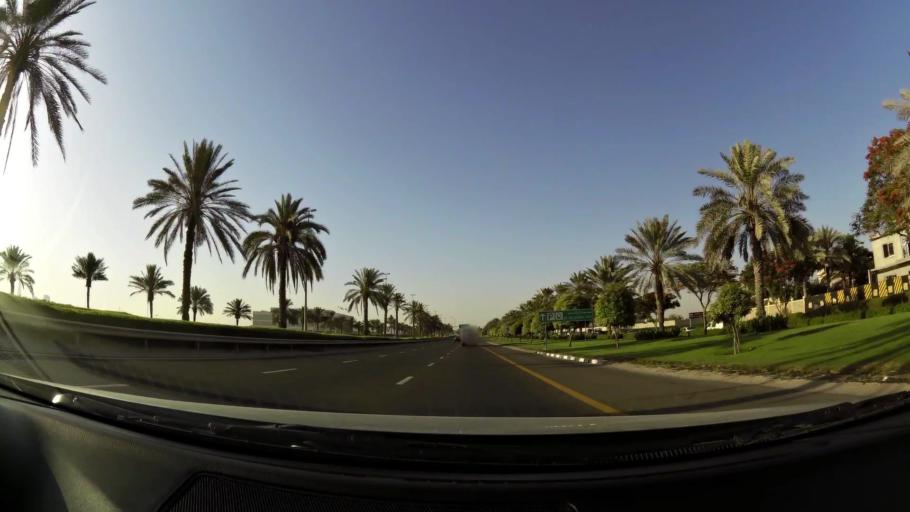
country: AE
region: Ash Shariqah
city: Sharjah
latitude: 25.1987
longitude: 55.3749
